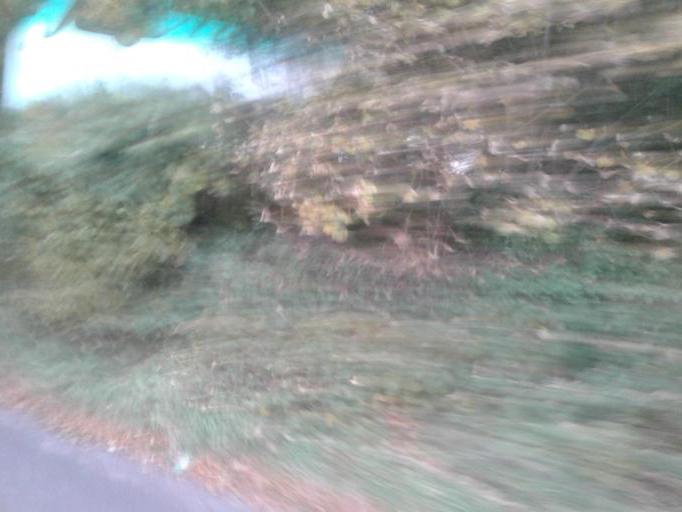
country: IE
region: Munster
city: Nenagh Bridge
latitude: 52.9544
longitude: -8.0338
